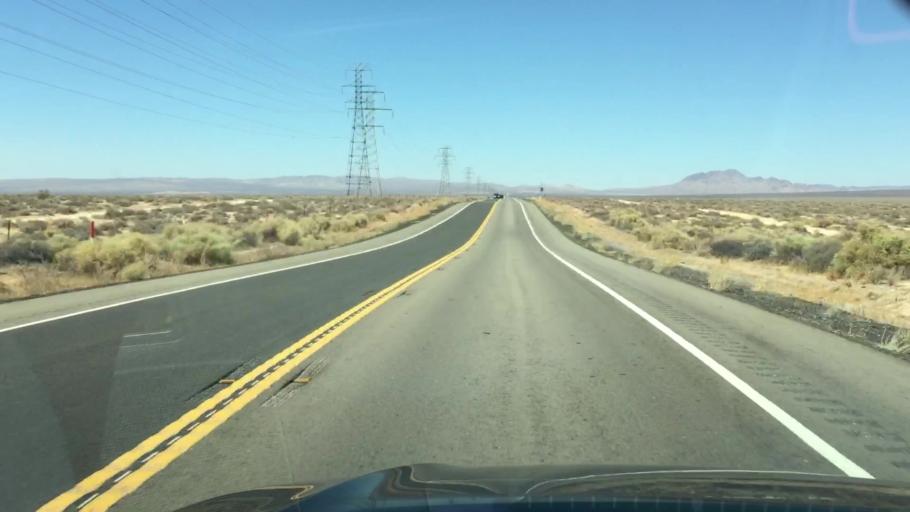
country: US
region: California
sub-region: Kern County
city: Boron
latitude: 35.1452
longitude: -117.5841
